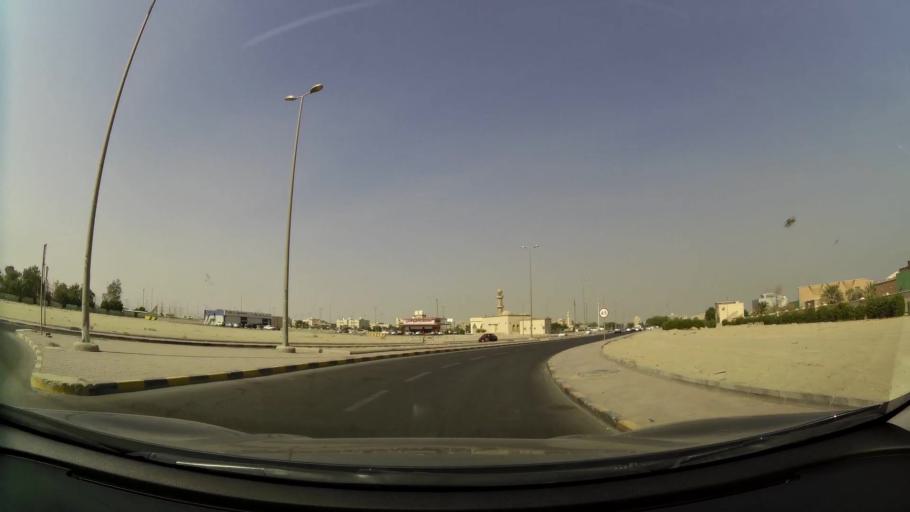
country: KW
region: Al Ahmadi
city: Al Ahmadi
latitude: 29.0889
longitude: 48.1058
